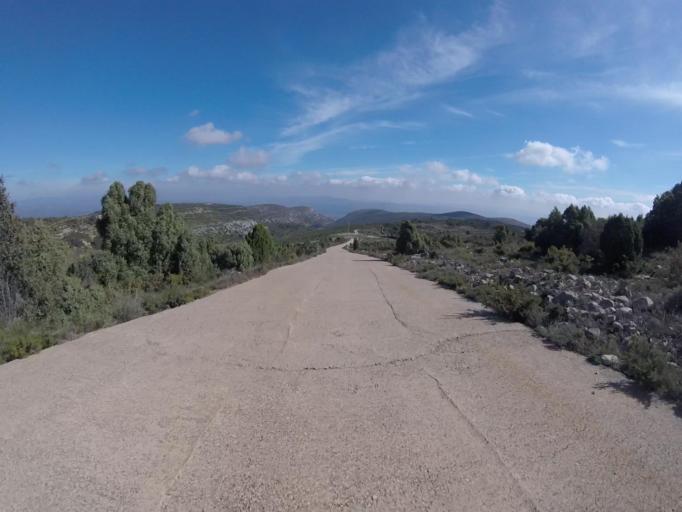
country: ES
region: Valencia
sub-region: Provincia de Castello
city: Sarratella
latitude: 40.3227
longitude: 0.0278
